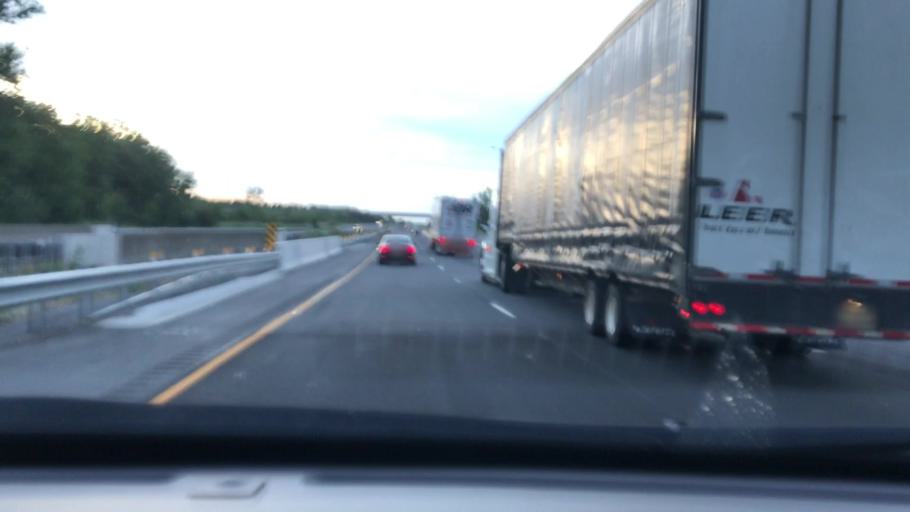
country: CA
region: Ontario
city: Niagara Falls
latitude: 43.0290
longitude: -79.1079
